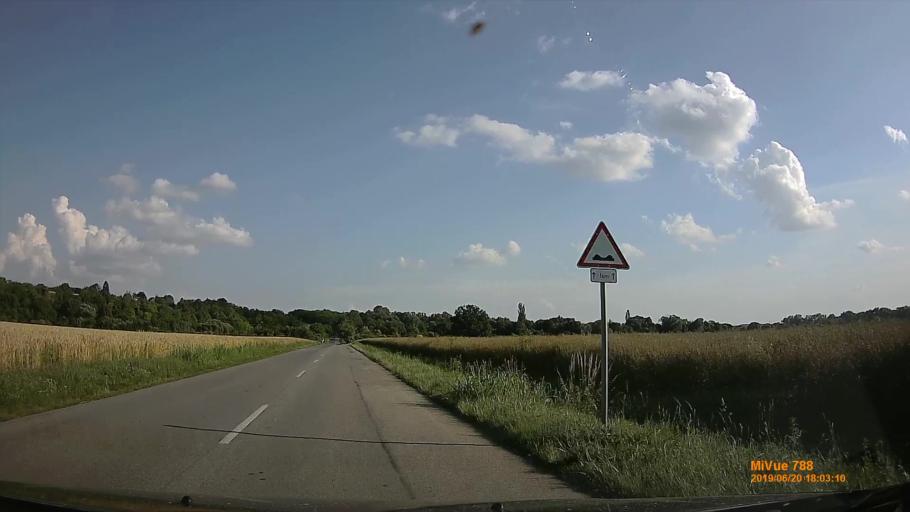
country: HU
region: Baranya
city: Szentlorinc
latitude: 46.0652
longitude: 17.9908
